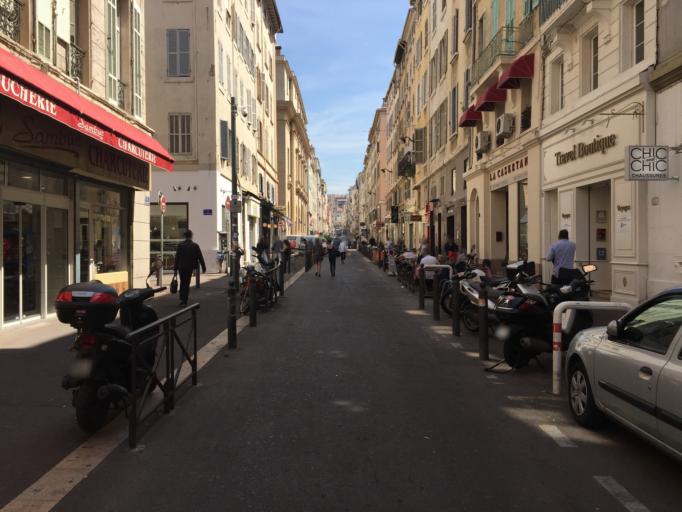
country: FR
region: Provence-Alpes-Cote d'Azur
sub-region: Departement des Bouches-du-Rhone
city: Marseille 02
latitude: 43.2929
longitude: 5.3750
